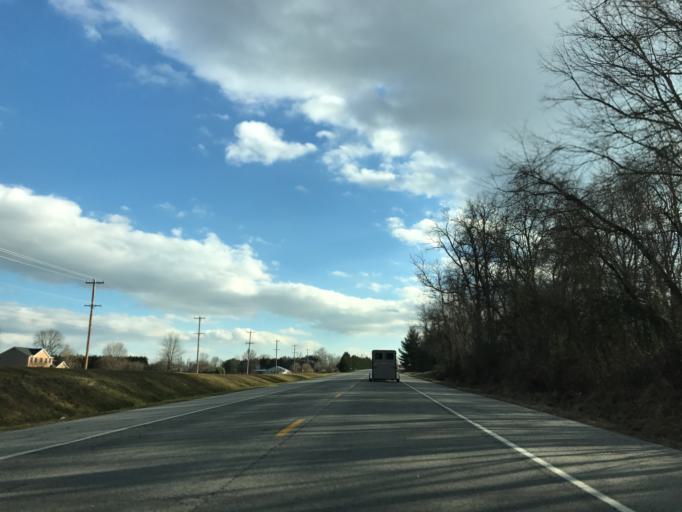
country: US
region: Maryland
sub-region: Cecil County
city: Rising Sun
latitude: 39.6437
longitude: -76.0724
